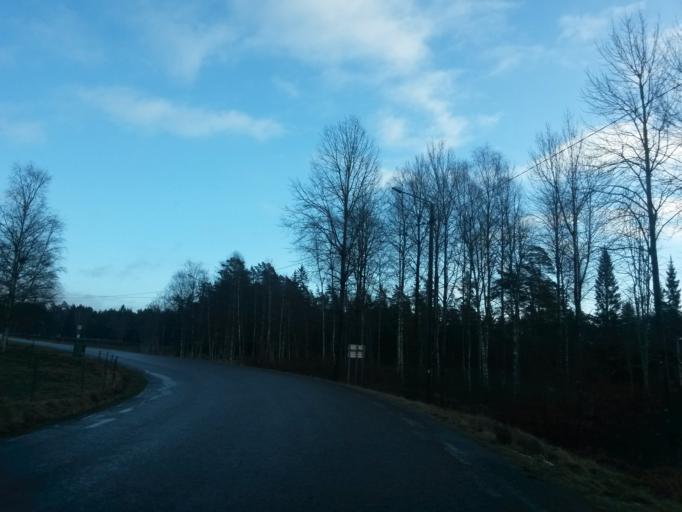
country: SE
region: Vaestra Goetaland
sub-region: Boras Kommun
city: Boras
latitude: 57.8577
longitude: 12.9282
